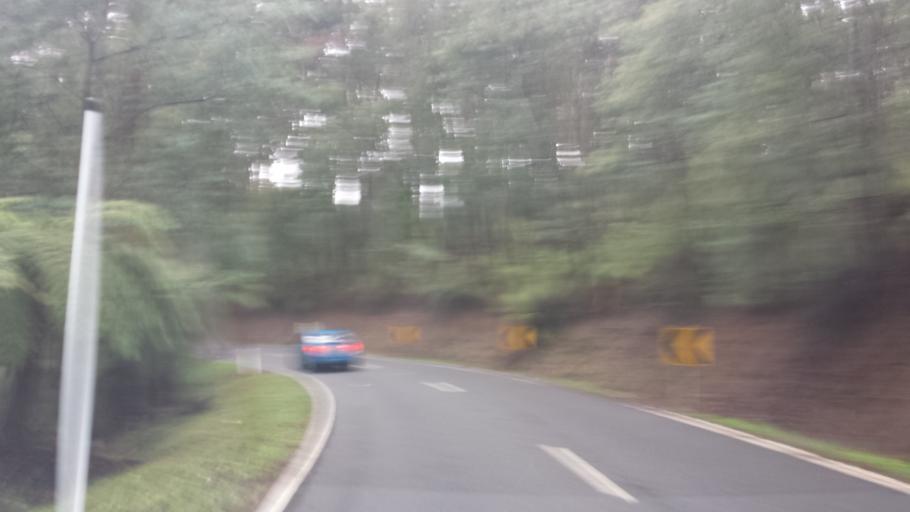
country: AU
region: Victoria
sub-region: Yarra Ranges
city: Monbulk
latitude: -37.8948
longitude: 145.4211
